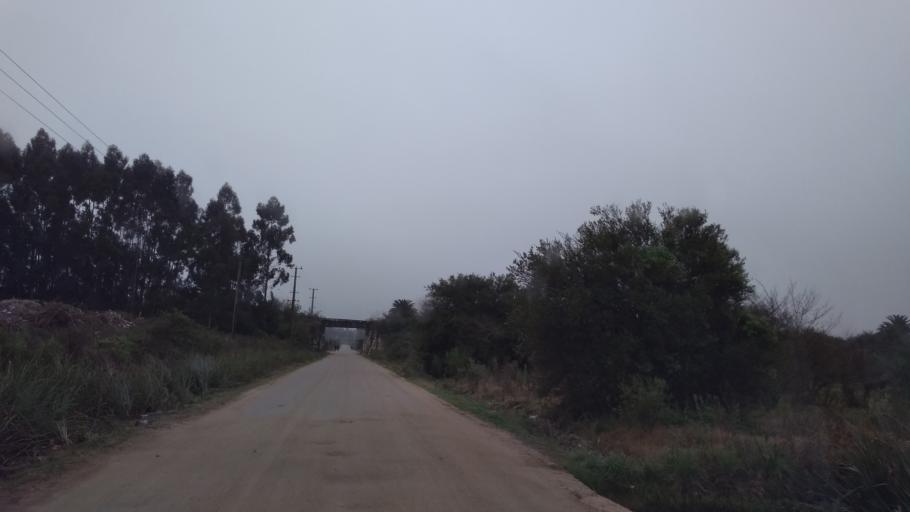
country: UY
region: Florida
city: Florida
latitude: -34.0876
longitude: -56.2075
